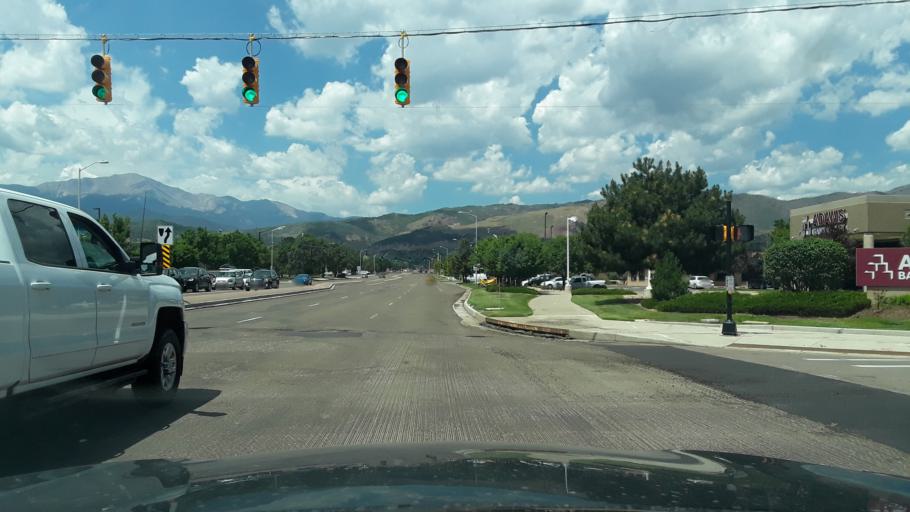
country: US
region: Colorado
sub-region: El Paso County
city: Colorado Springs
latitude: 38.8968
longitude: -104.8520
